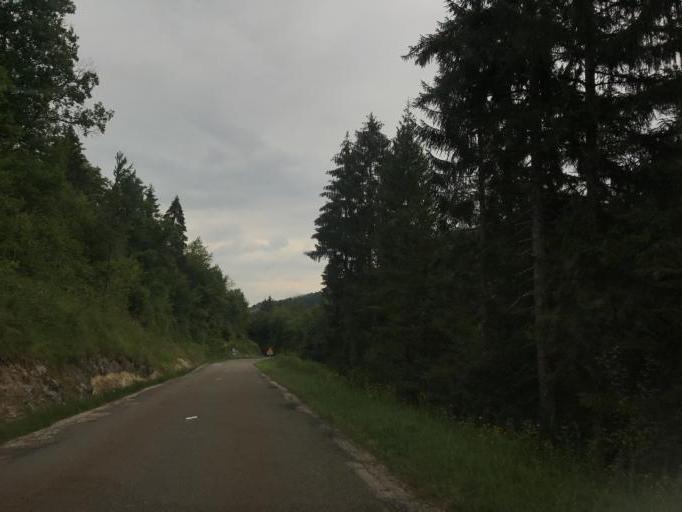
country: FR
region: Franche-Comte
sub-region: Departement du Jura
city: Lavans-les-Saint-Claude
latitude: 46.3268
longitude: 5.7604
